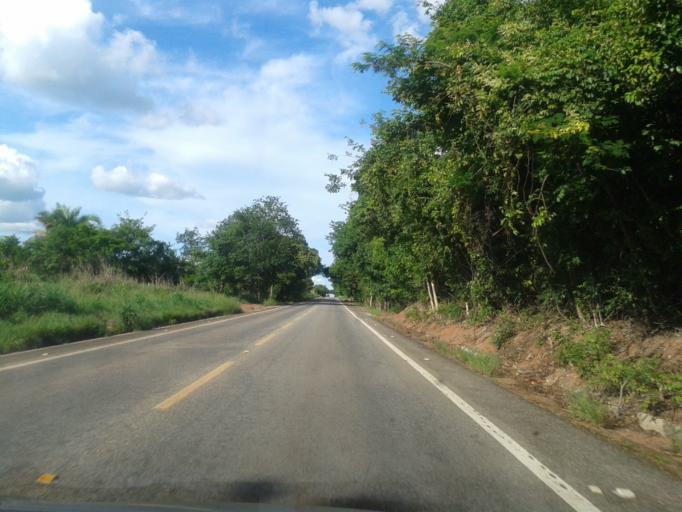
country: BR
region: Goias
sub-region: Mozarlandia
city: Mozarlandia
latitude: -14.4843
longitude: -50.4784
